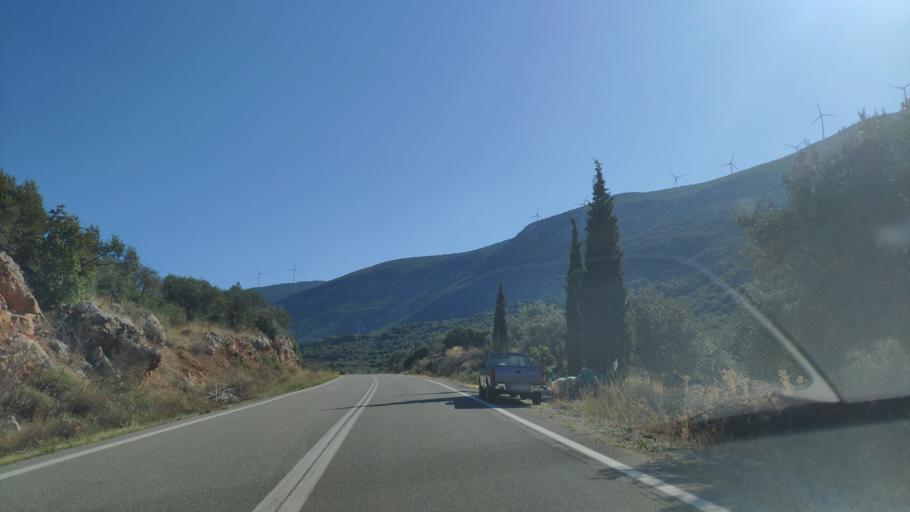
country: GR
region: Peloponnese
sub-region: Nomos Argolidos
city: Palaia Epidavros
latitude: 37.5717
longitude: 23.2496
